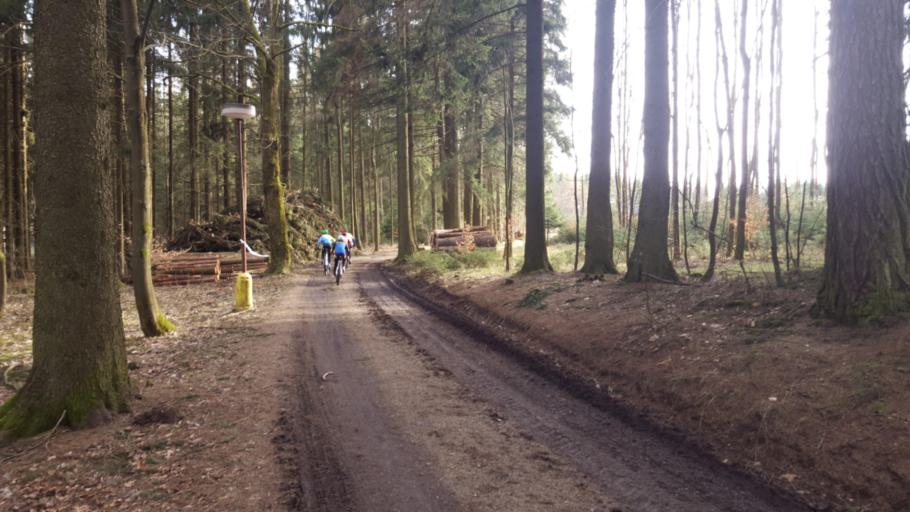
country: CZ
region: Karlovarsky
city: As
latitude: 50.2316
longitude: 12.2065
